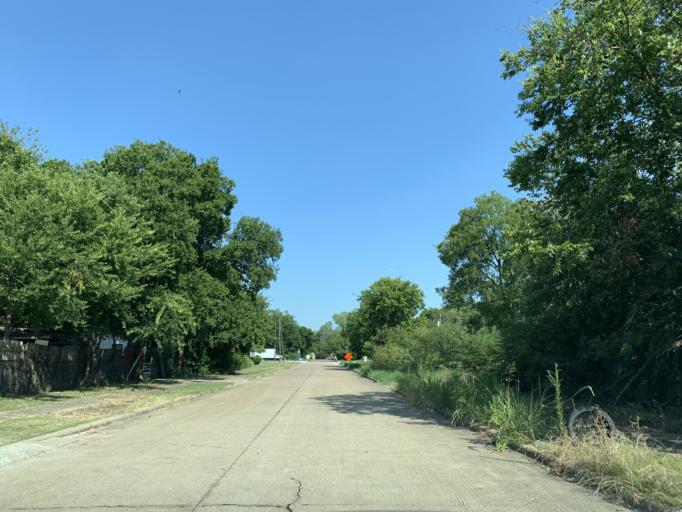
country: US
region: Texas
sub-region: Dallas County
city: Hutchins
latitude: 32.6547
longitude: -96.7711
